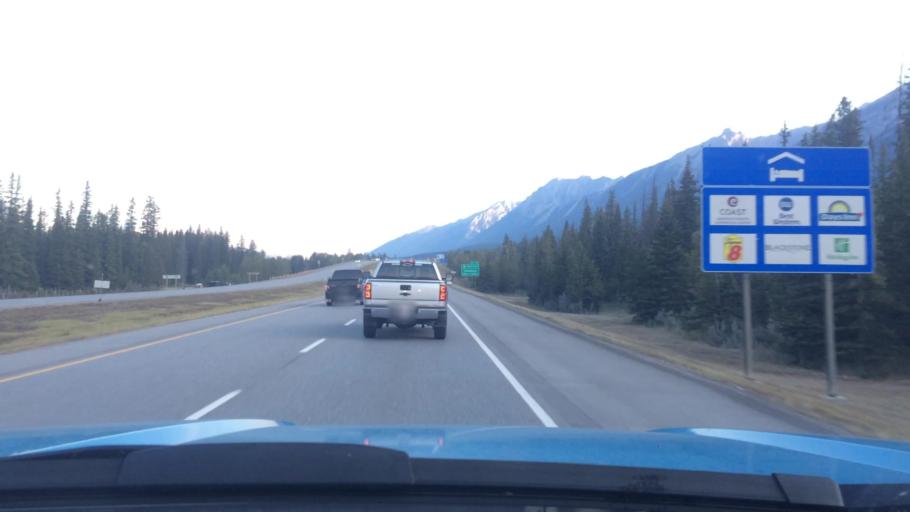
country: CA
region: Alberta
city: Canmore
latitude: 51.0697
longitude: -115.3275
